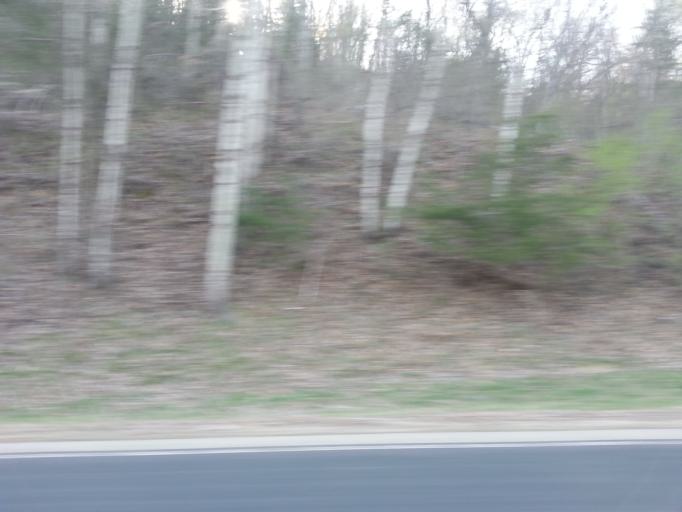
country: US
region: Minnesota
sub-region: Goodhue County
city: Red Wing
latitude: 44.6492
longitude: -92.6135
